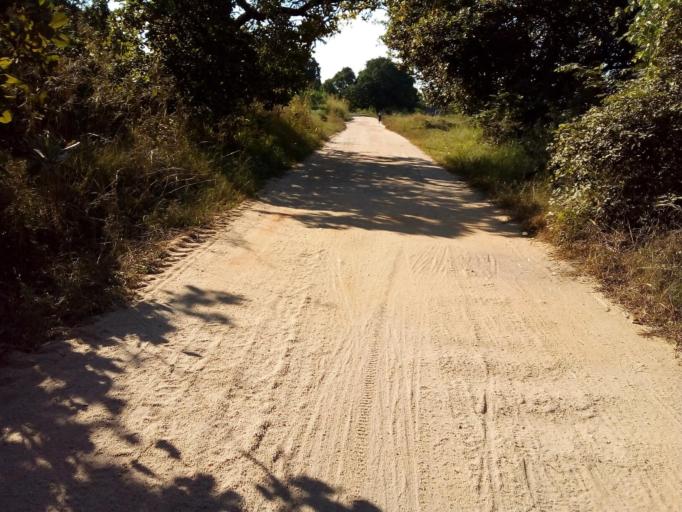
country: MZ
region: Zambezia
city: Quelimane
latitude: -17.5264
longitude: 36.6165
